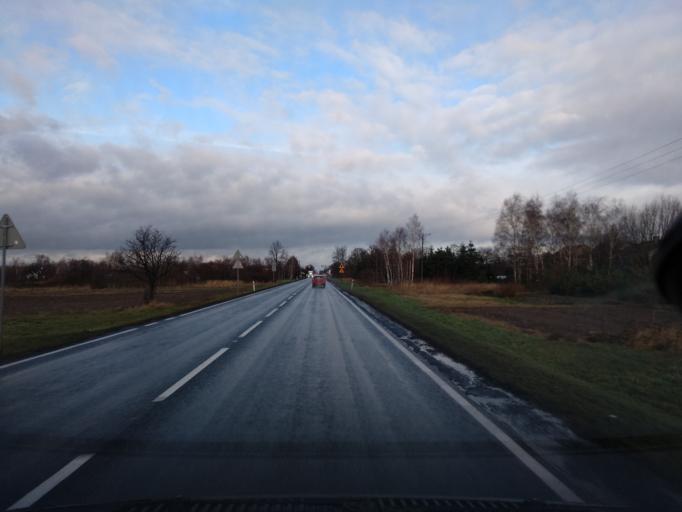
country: PL
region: Greater Poland Voivodeship
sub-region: Powiat koninski
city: Rychwal
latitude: 52.0752
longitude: 18.1590
